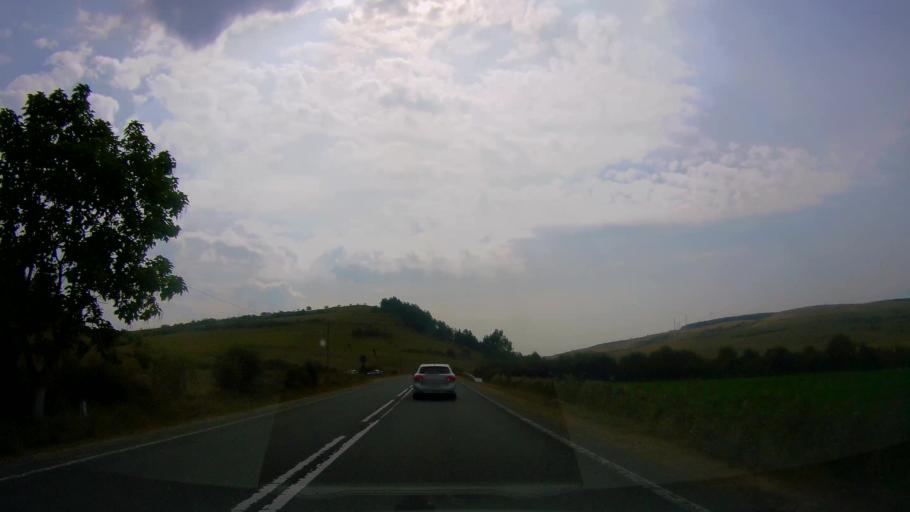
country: RO
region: Cluj
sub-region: Comuna Sanpaul
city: Sanpaul
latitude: 46.8388
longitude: 23.4066
